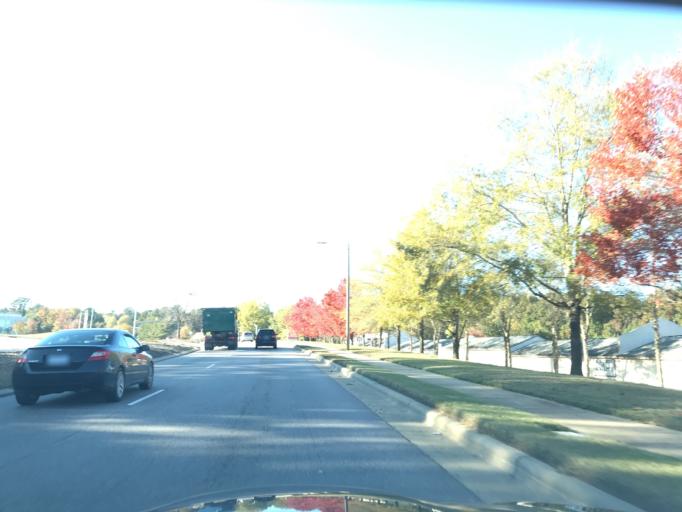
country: US
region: North Carolina
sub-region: Wake County
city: Garner
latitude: 35.7673
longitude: -78.5615
